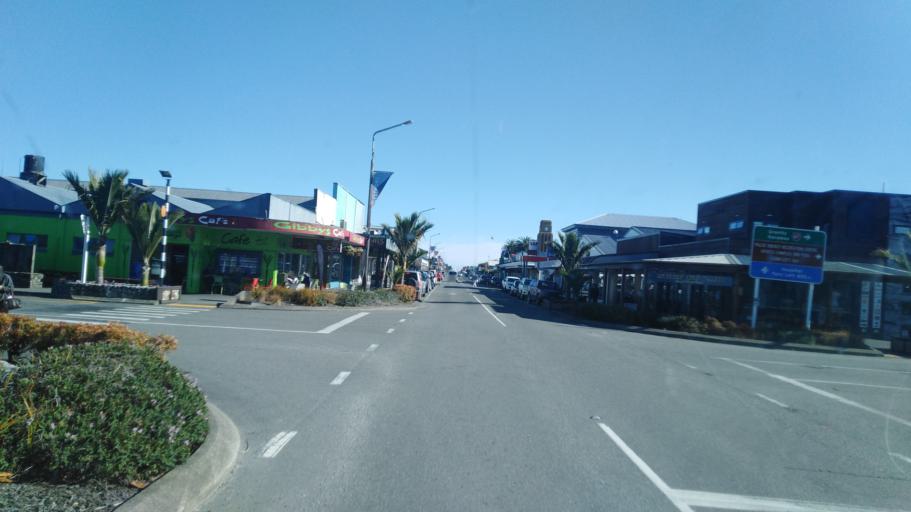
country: NZ
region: West Coast
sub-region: Buller District
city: Westport
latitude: -41.7555
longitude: 171.5987
